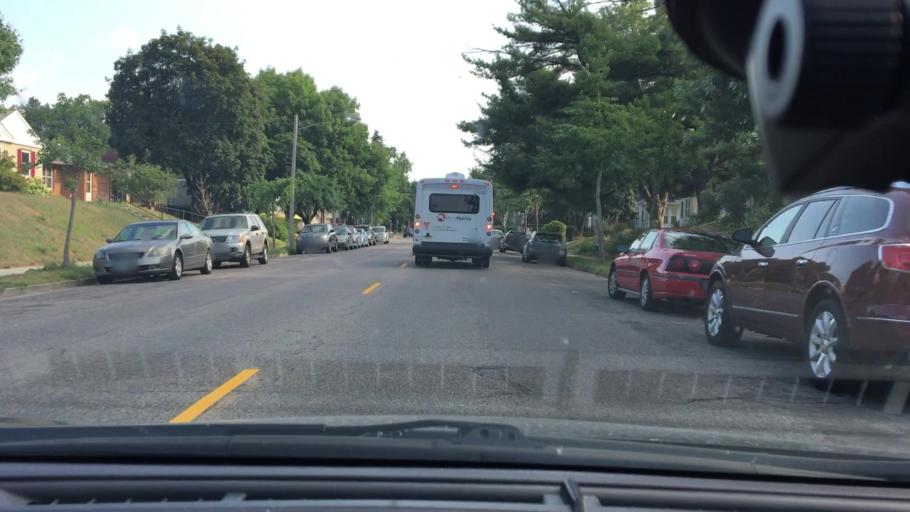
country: US
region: Minnesota
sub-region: Hennepin County
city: Richfield
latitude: 44.9207
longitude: -93.2524
